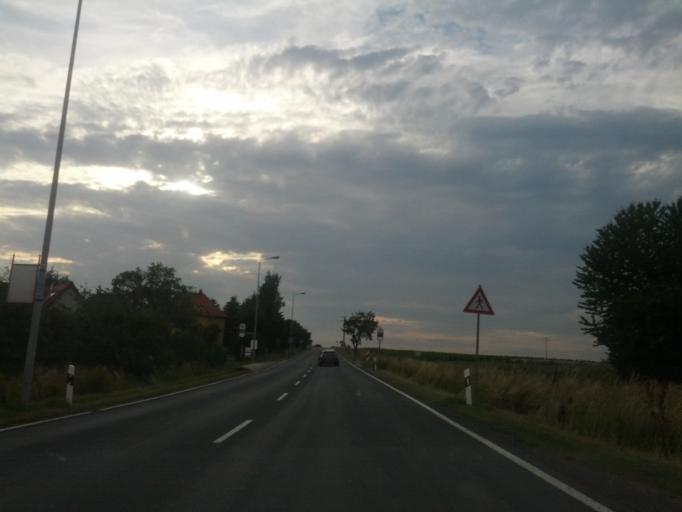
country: DE
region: Thuringia
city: Ingersleben
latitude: 50.9567
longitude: 10.9673
